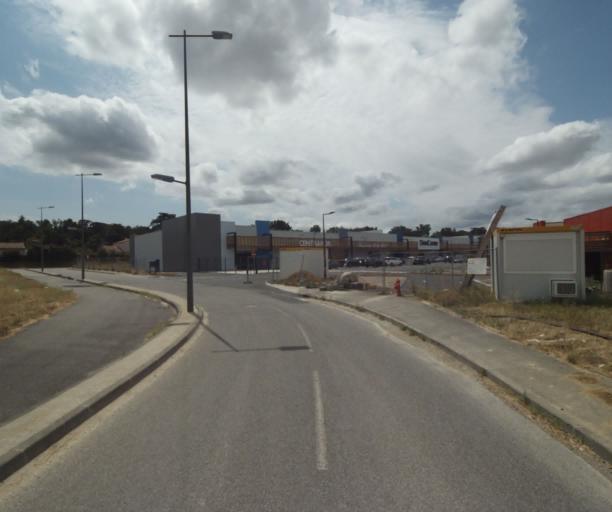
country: FR
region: Midi-Pyrenees
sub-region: Departement de la Haute-Garonne
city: Revel
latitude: 43.4524
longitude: 1.9934
